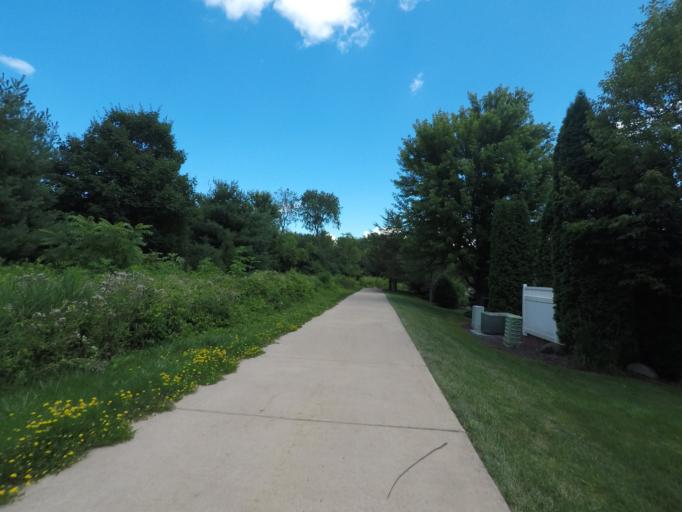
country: US
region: Wisconsin
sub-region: Dane County
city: Middleton
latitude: 43.0725
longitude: -89.5353
